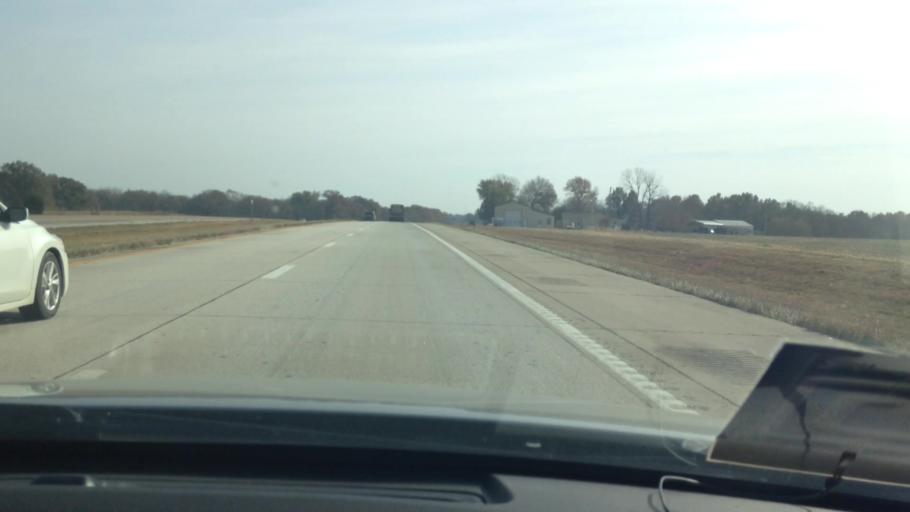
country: US
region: Missouri
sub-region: Henry County
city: Clinton
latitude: 38.4049
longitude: -93.8428
